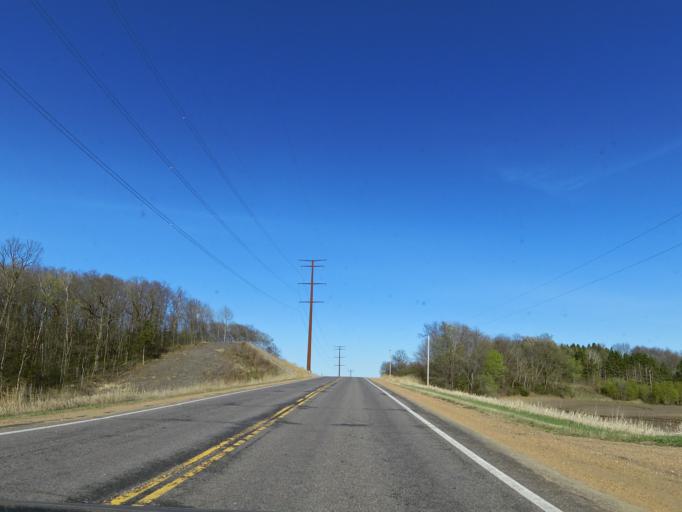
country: US
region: Minnesota
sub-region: Rice County
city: Lonsdale
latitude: 44.5727
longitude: -93.4529
